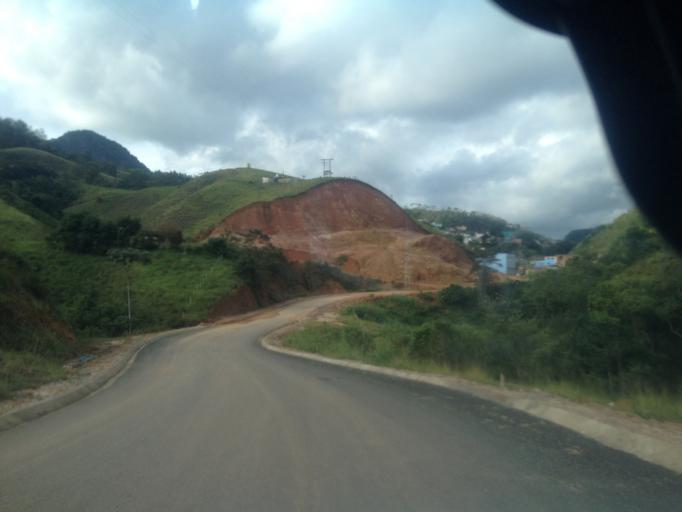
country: BR
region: Rio de Janeiro
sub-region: Quatis
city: Quatis
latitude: -22.2087
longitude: -44.2399
